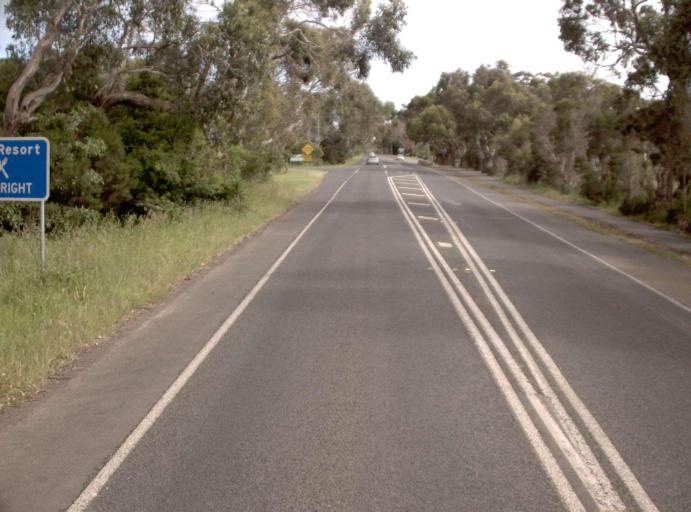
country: AU
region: Victoria
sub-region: Bass Coast
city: Phillip Island
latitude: -38.4746
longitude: 145.2390
